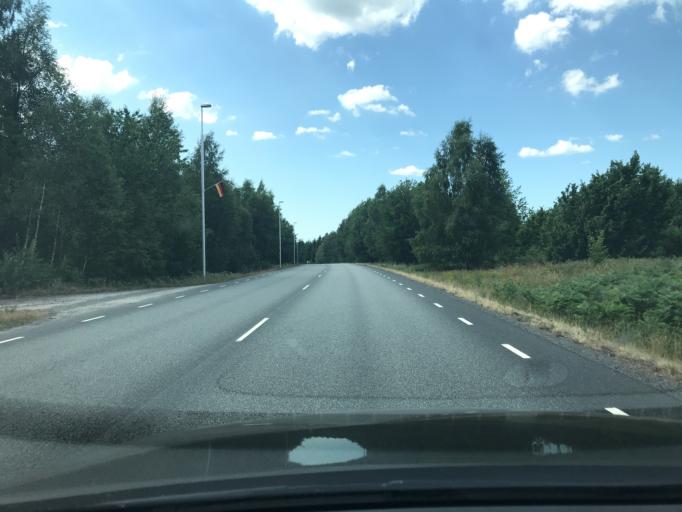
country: SE
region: Skane
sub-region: Hassleholms Kommun
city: Hastveda
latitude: 56.2739
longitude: 13.9506
